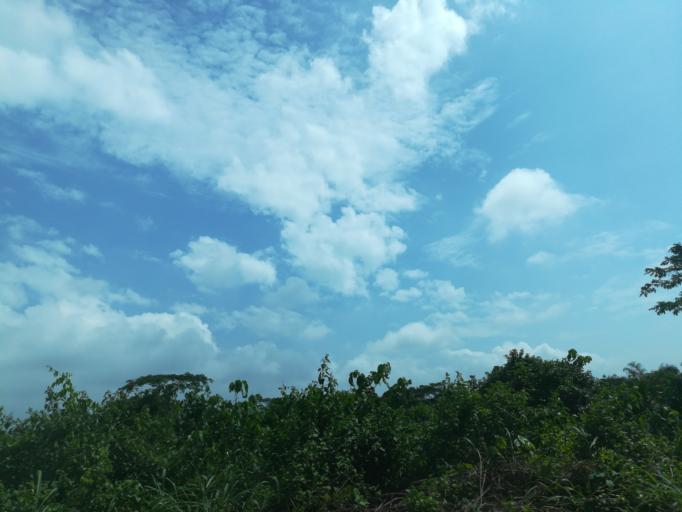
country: NG
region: Lagos
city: Ikorodu
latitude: 6.6581
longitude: 3.6858
